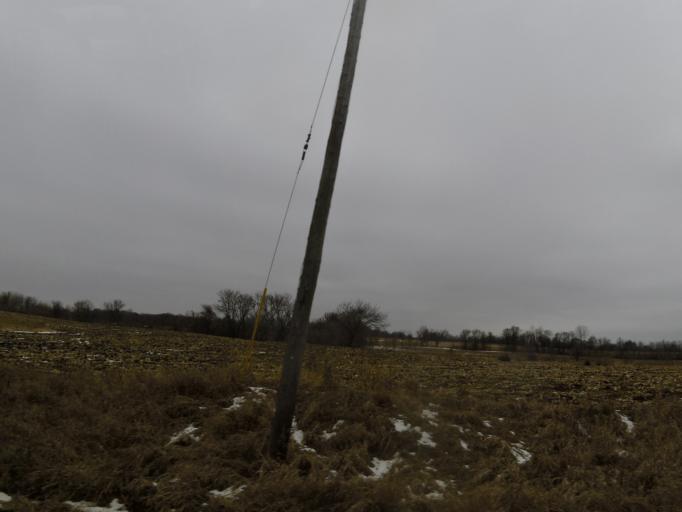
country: US
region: Minnesota
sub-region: Wright County
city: Montrose
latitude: 45.0314
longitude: -93.8584
